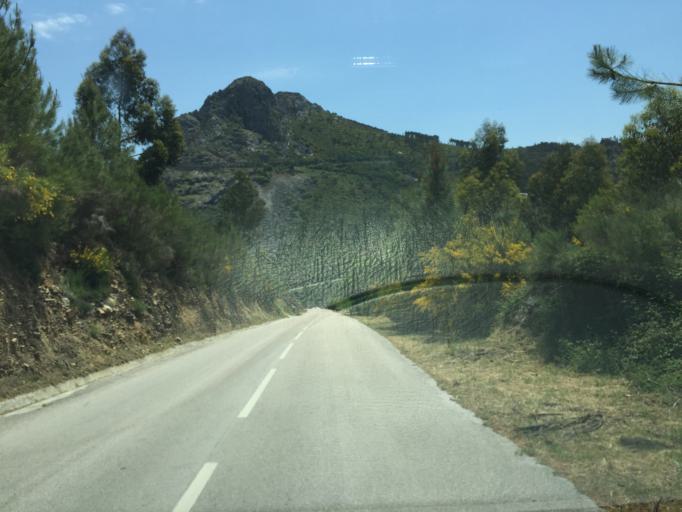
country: PT
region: Coimbra
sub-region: Pampilhosa da Serra
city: Pampilhosa da Serra
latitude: 40.0911
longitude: -7.8657
